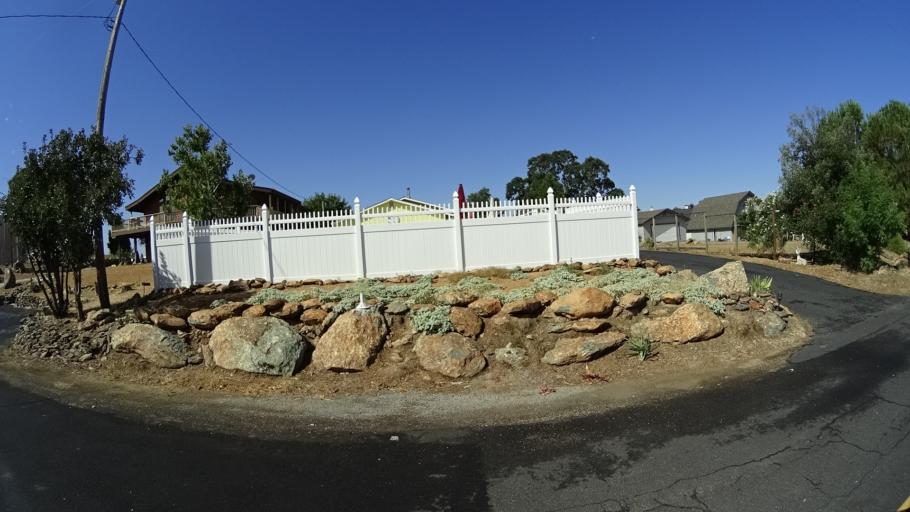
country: US
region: California
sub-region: Calaveras County
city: Copperopolis
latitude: 37.9130
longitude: -120.6136
